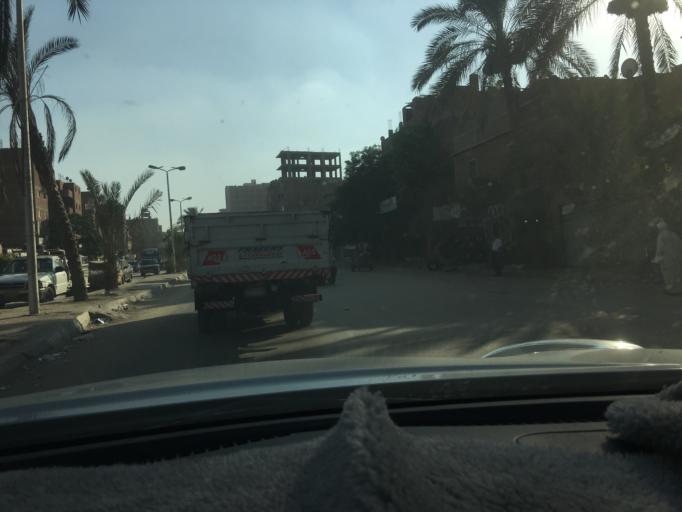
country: EG
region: Muhafazat al Qalyubiyah
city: Al Khankah
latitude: 30.1489
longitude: 31.3667
